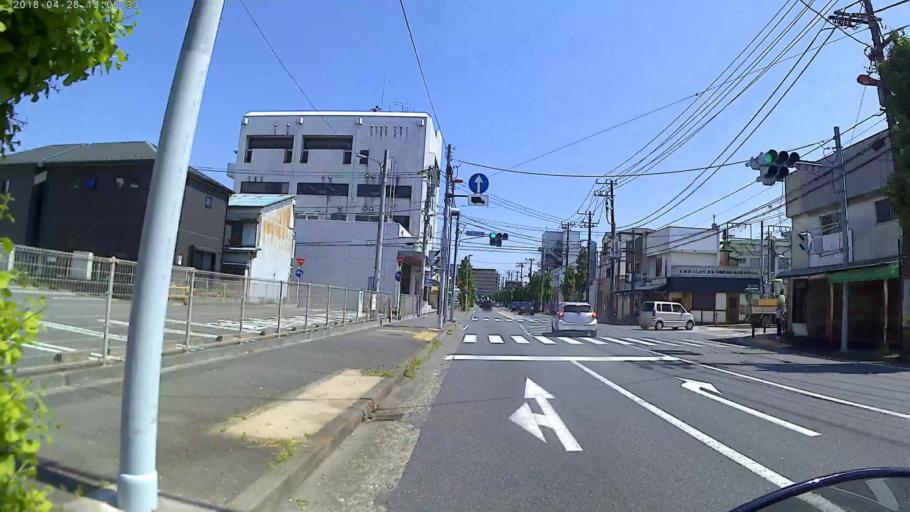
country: JP
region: Kanagawa
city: Yokosuka
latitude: 35.2489
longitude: 139.6815
